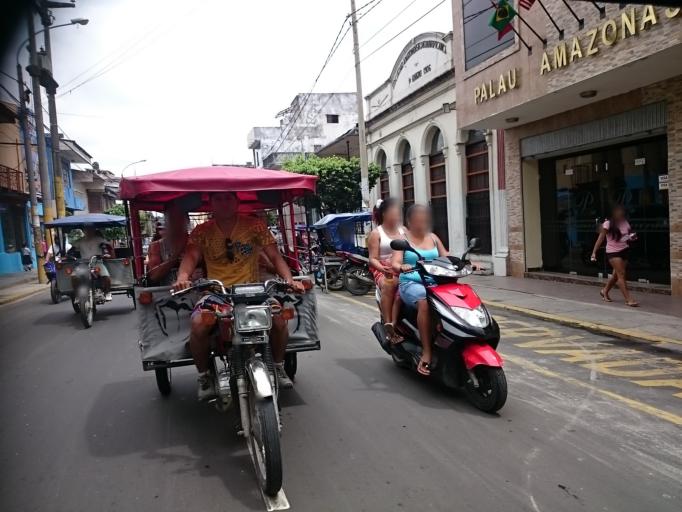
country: PE
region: Loreto
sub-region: Provincia de Maynas
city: Iquitos
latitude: -3.7505
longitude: -73.2469
